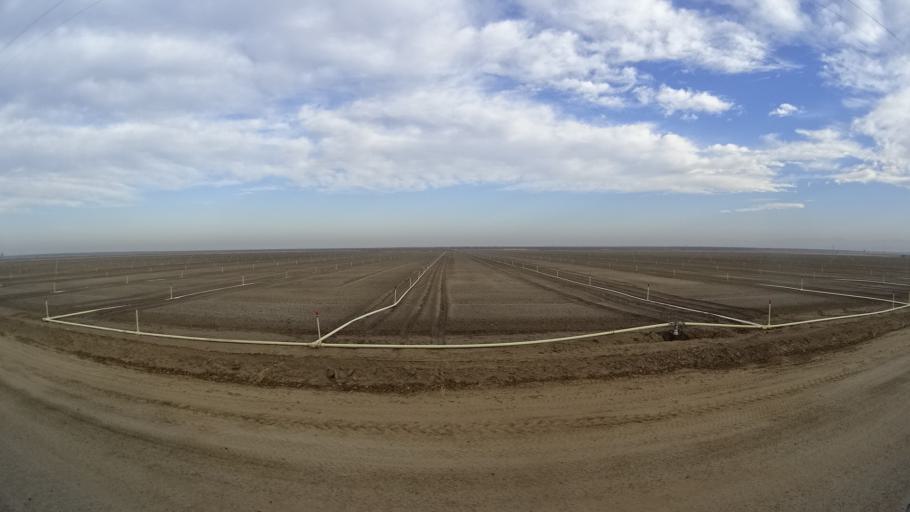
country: US
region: California
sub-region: Kern County
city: Rosedale
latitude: 35.4125
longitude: -119.1865
